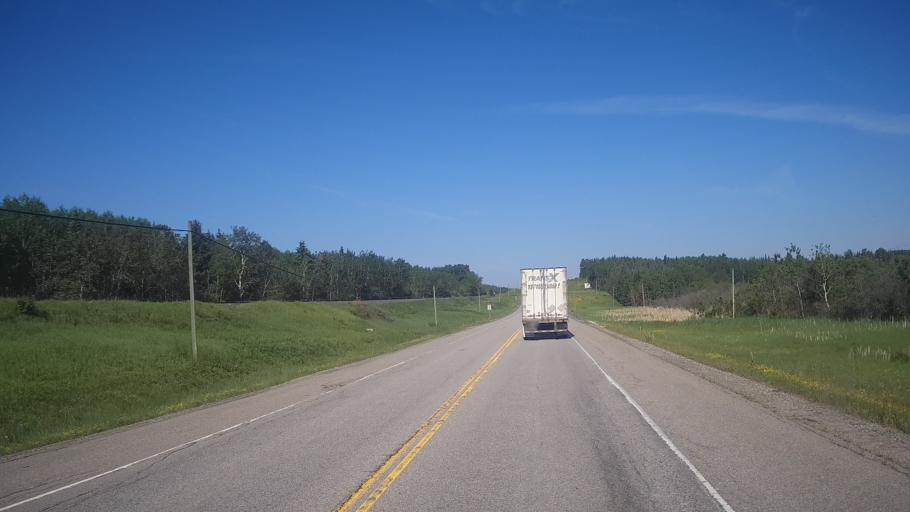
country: CA
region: Ontario
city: Dryden
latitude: 49.6899
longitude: -92.5144
